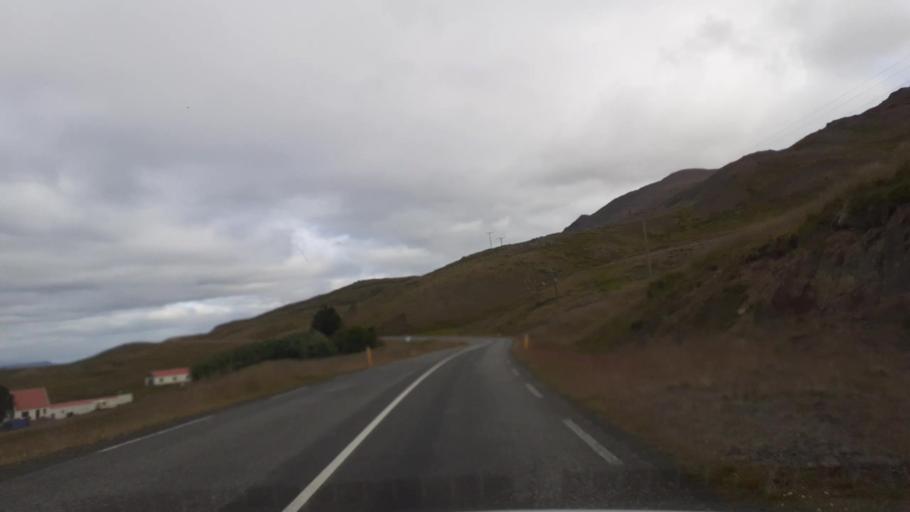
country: IS
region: Northeast
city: Akureyri
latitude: 65.8204
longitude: -18.0501
